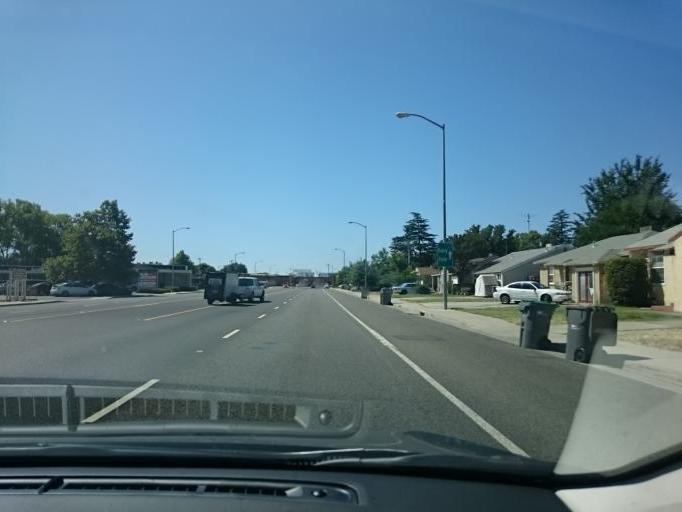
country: US
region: California
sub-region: Yolo County
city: West Sacramento
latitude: 38.5741
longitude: -121.5242
